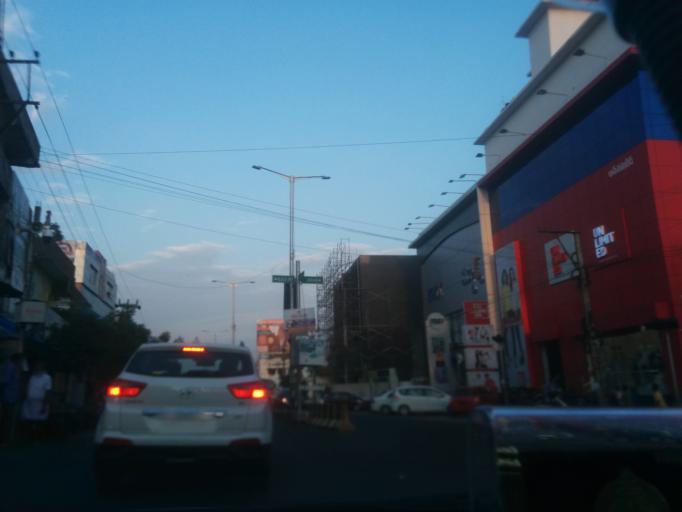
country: IN
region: Andhra Pradesh
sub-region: East Godavari
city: Rajahmundry
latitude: 17.0078
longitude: 81.7920
